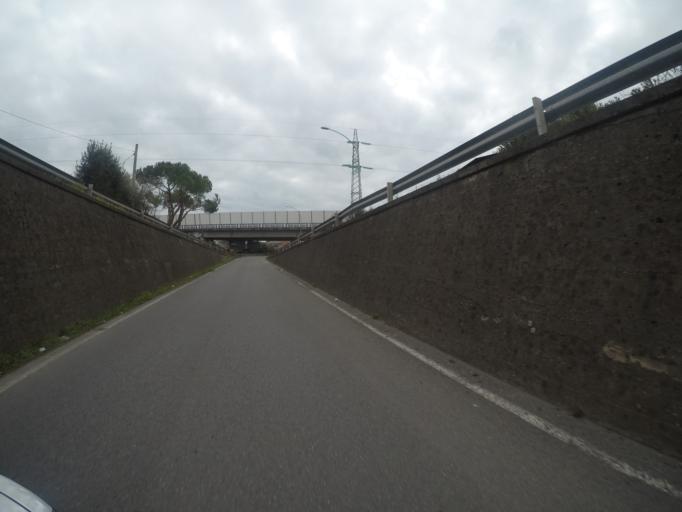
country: IT
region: Tuscany
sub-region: Provincia di Massa-Carrara
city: Massa
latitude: 44.0199
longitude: 10.1145
